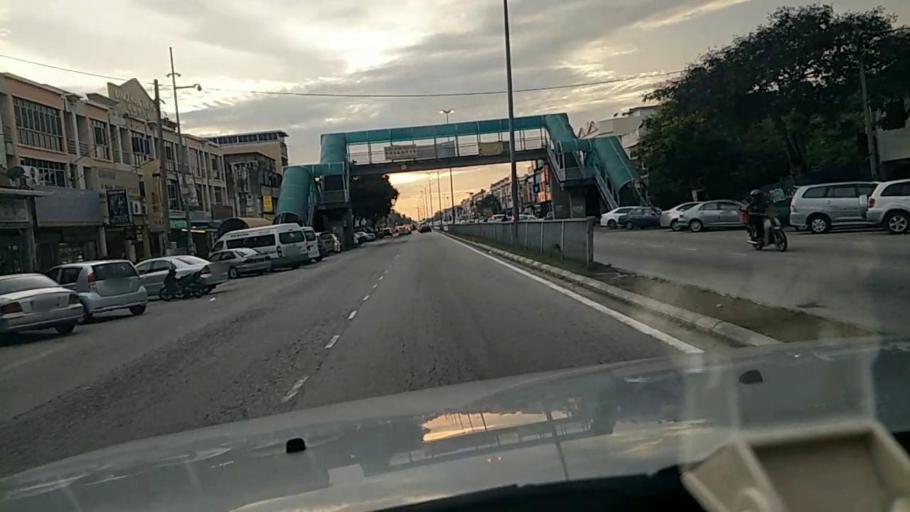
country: MY
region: Perak
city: Kampong Dungun
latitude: 3.1374
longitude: 101.3735
